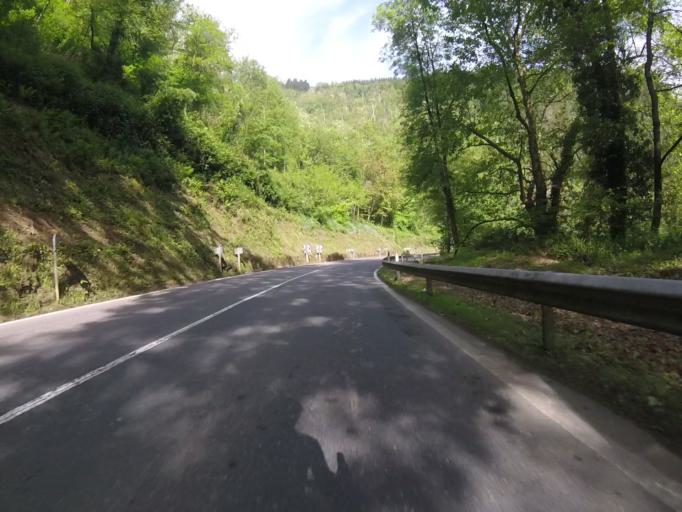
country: ES
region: Basque Country
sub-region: Provincia de Guipuzcoa
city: Azkoitia
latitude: 43.1517
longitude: -2.3441
